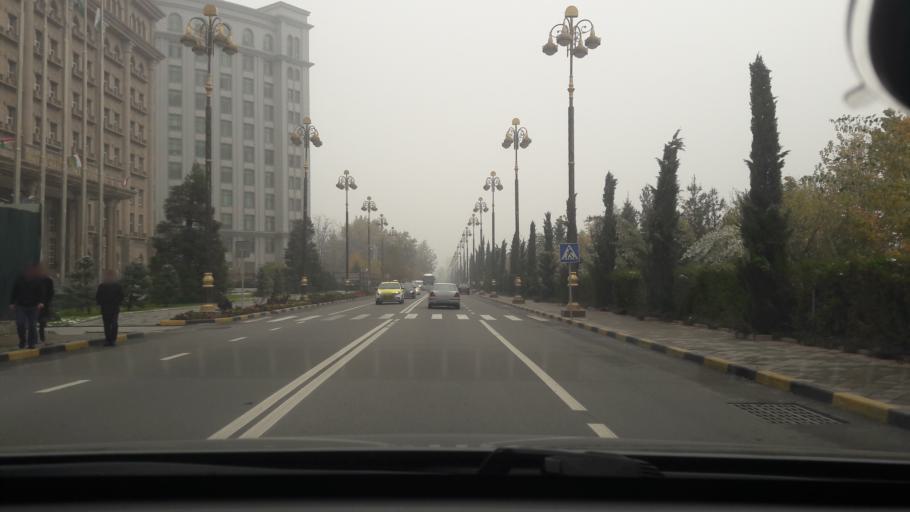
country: TJ
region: Dushanbe
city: Dushanbe
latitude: 38.5800
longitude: 68.7822
